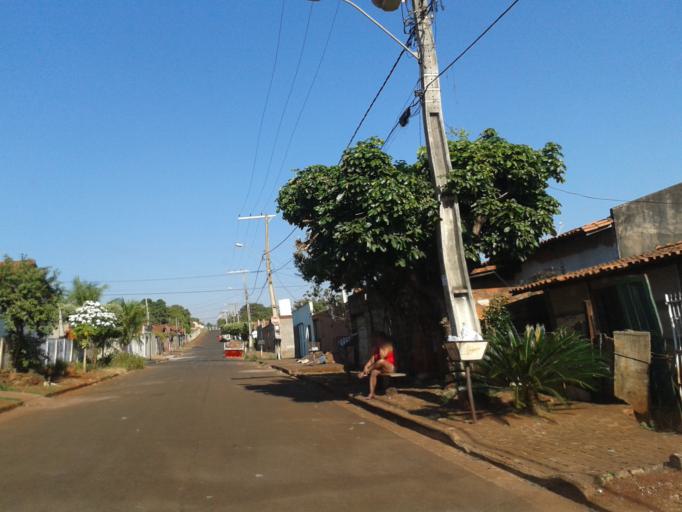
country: BR
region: Minas Gerais
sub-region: Ituiutaba
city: Ituiutaba
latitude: -18.9676
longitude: -49.4776
